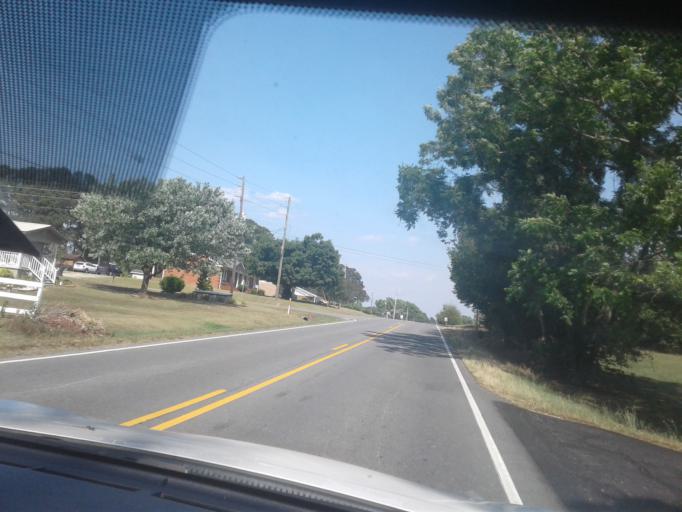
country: US
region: North Carolina
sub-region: Johnston County
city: Benson
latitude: 35.3883
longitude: -78.5687
